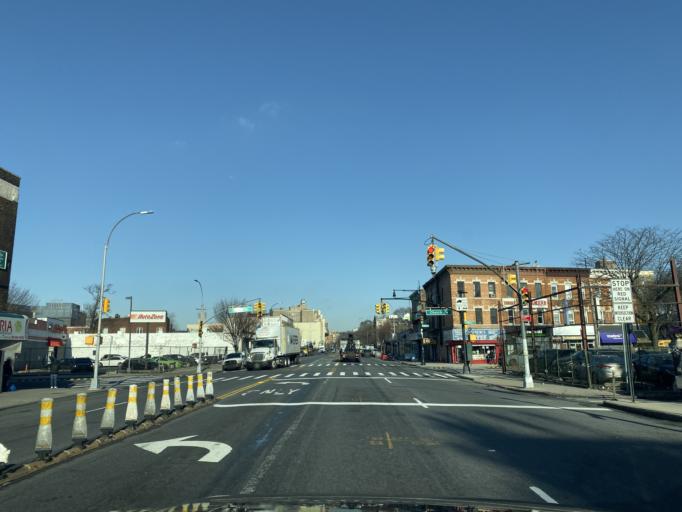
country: US
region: New York
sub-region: Kings County
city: Brooklyn
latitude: 40.6460
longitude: -73.9707
